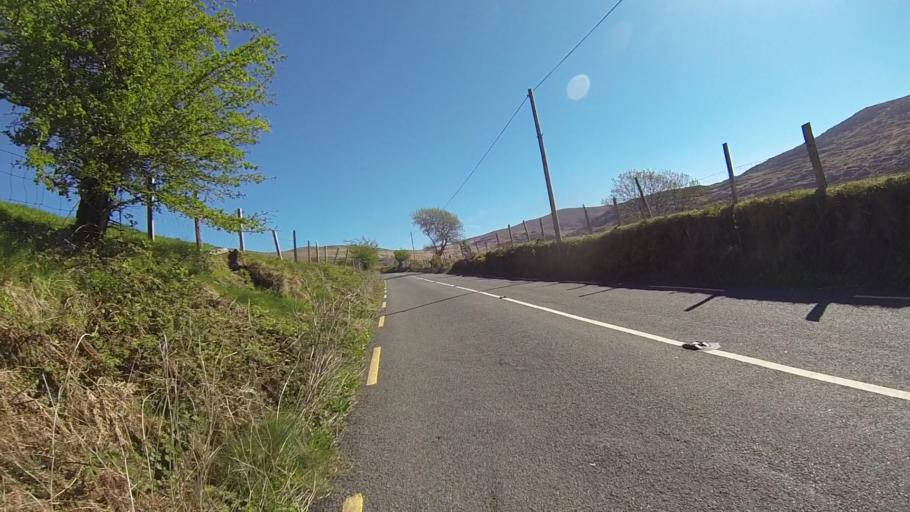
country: IE
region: Munster
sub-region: Ciarrai
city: Kenmare
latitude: 51.7750
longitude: -9.7321
